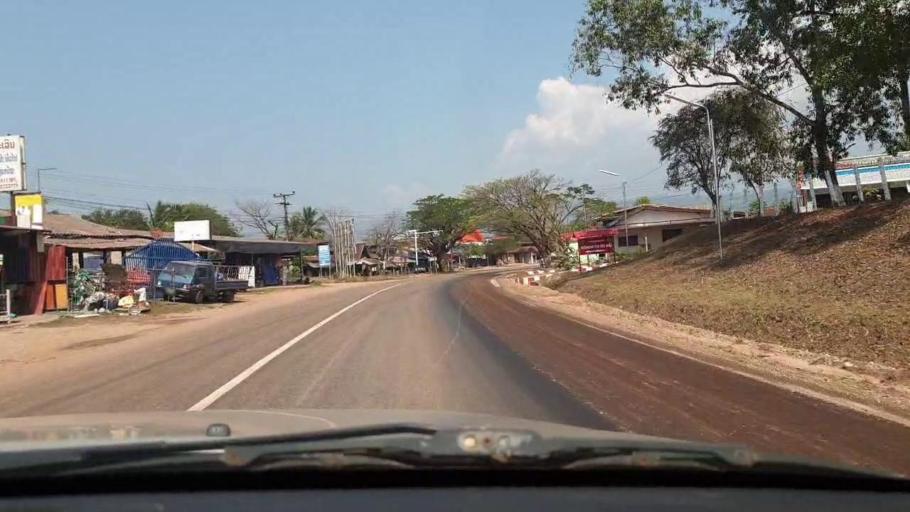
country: TH
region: Nong Khai
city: Rattanawapi
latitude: 18.1818
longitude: 103.0551
